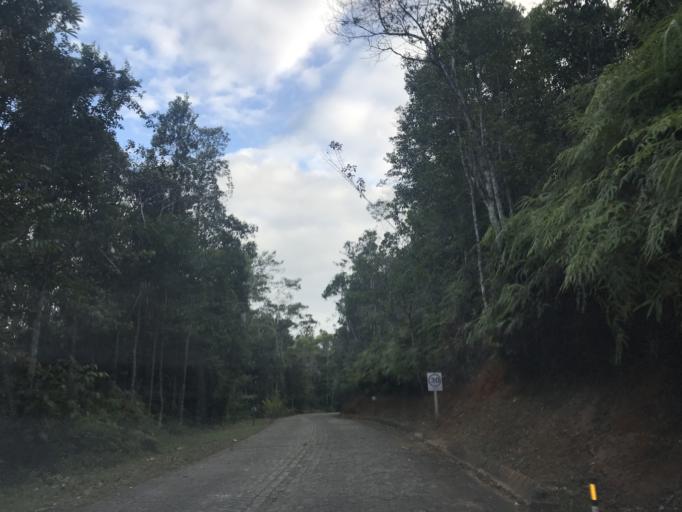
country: BR
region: Bahia
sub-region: Gandu
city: Gandu
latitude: -13.9098
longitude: -39.4610
